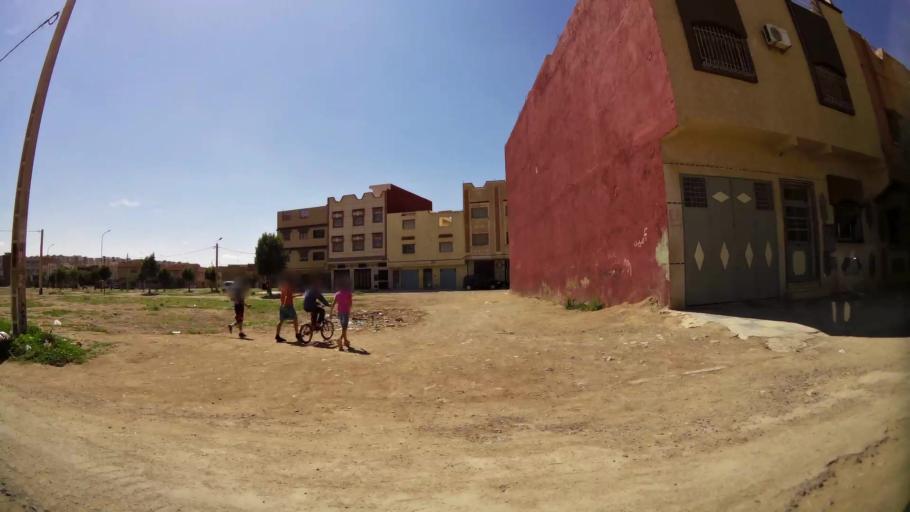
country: MA
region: Oriental
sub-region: Oujda-Angad
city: Oujda
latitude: 34.6662
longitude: -1.9290
